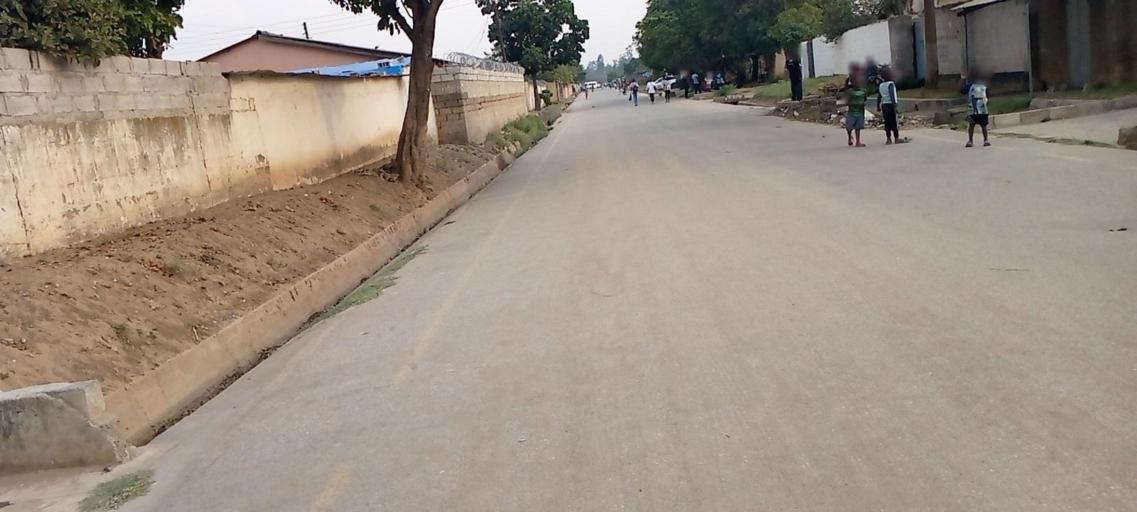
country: ZM
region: Lusaka
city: Lusaka
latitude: -15.4018
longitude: 28.3444
